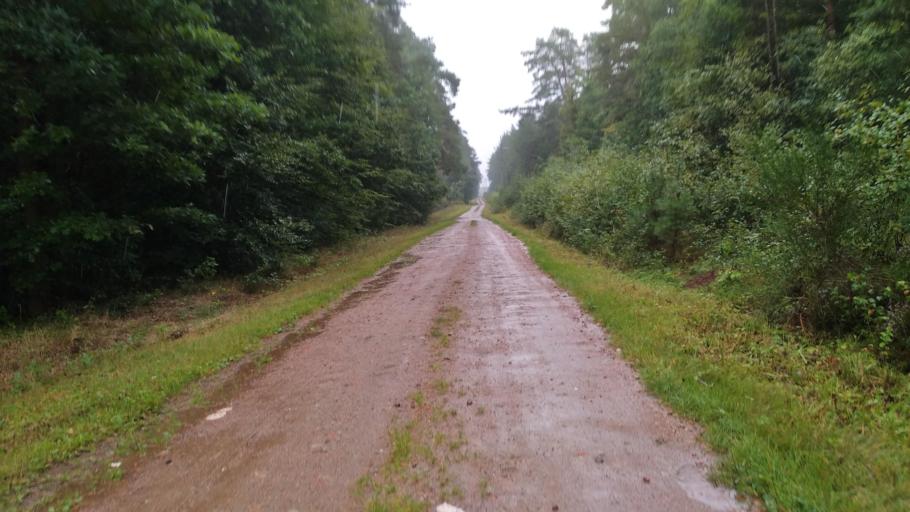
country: PL
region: Pomeranian Voivodeship
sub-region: Powiat wejherowski
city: Goscicino
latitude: 54.6221
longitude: 18.1496
